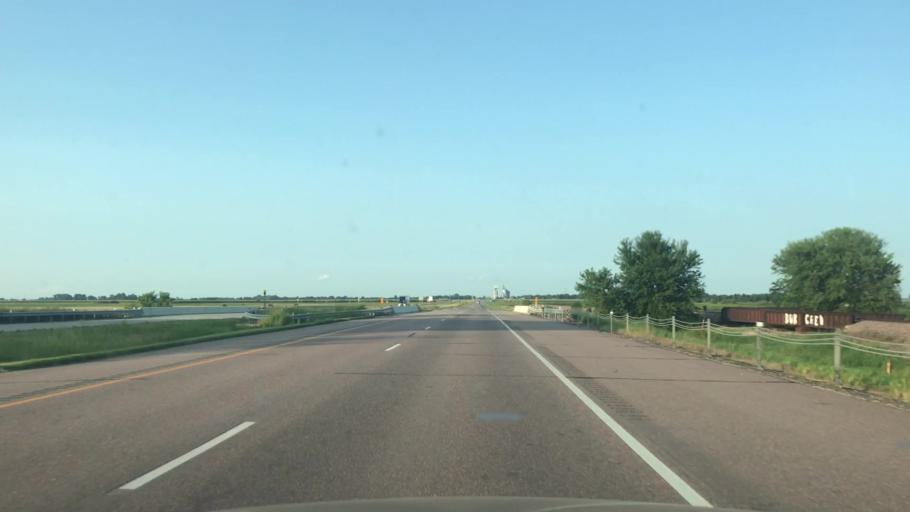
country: US
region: Minnesota
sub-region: Jackson County
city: Lakefield
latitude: 43.7758
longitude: -95.3524
